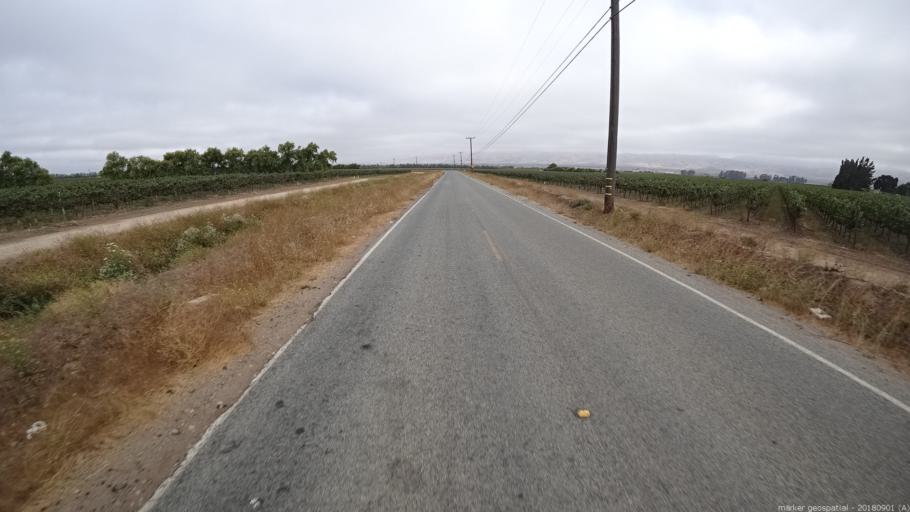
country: US
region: California
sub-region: Monterey County
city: Soledad
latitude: 36.3582
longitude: -121.3205
